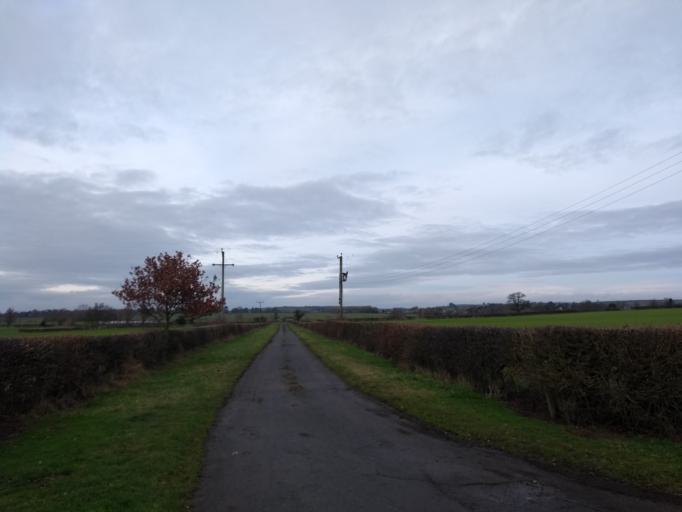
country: GB
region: England
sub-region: East Riding of Yorkshire
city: Stamford Bridge
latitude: 54.0643
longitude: -0.9302
